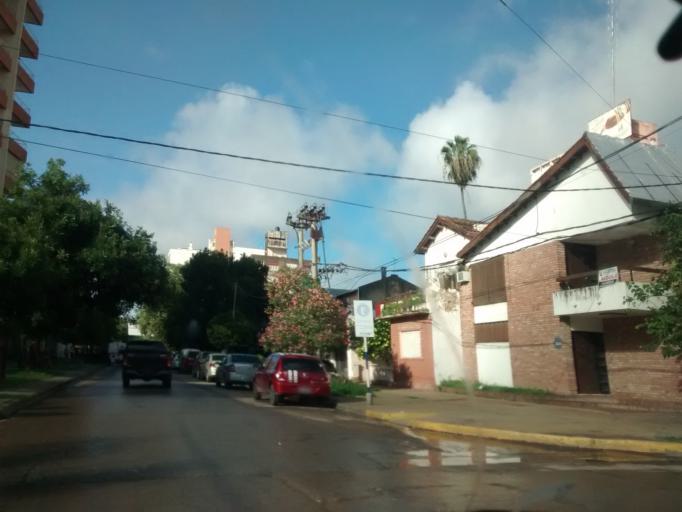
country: AR
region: Chaco
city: Resistencia
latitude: -27.4534
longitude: -58.9821
